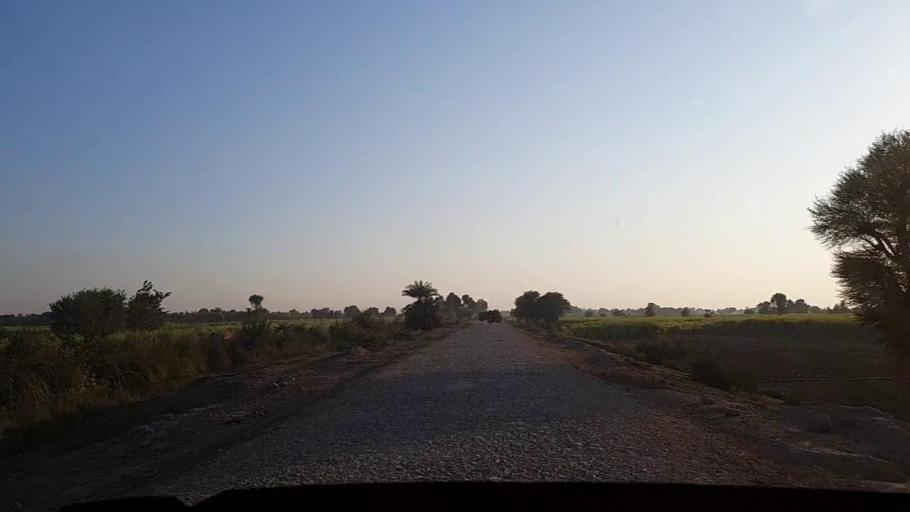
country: PK
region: Sindh
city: Sobhadero
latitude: 27.3735
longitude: 68.3787
